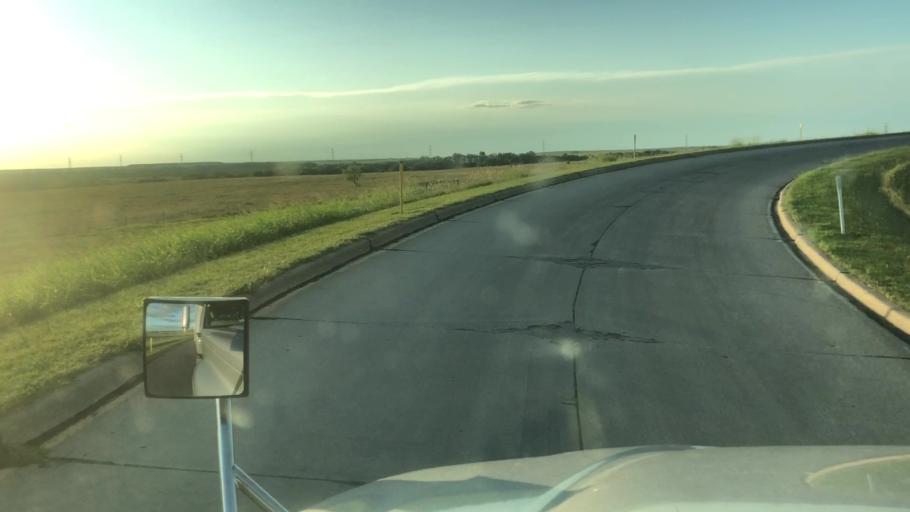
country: US
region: Oklahoma
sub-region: Noble County
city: Perry
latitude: 36.3842
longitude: -97.0692
